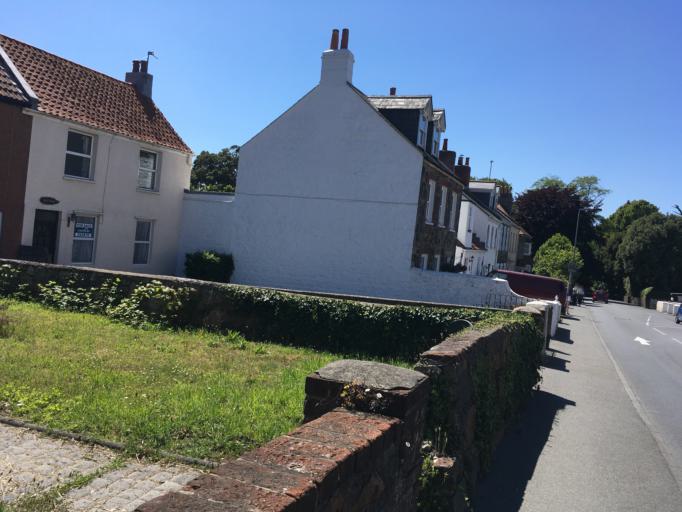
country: GG
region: St Peter Port
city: Saint Peter Port
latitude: 49.4601
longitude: -2.5596
